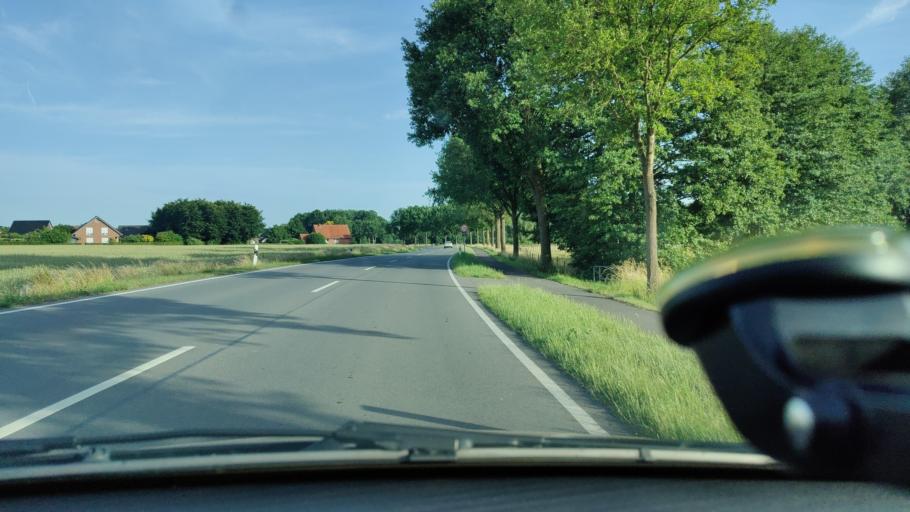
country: DE
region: North Rhine-Westphalia
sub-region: Regierungsbezirk Munster
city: Billerbeck
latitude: 51.9845
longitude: 7.2740
